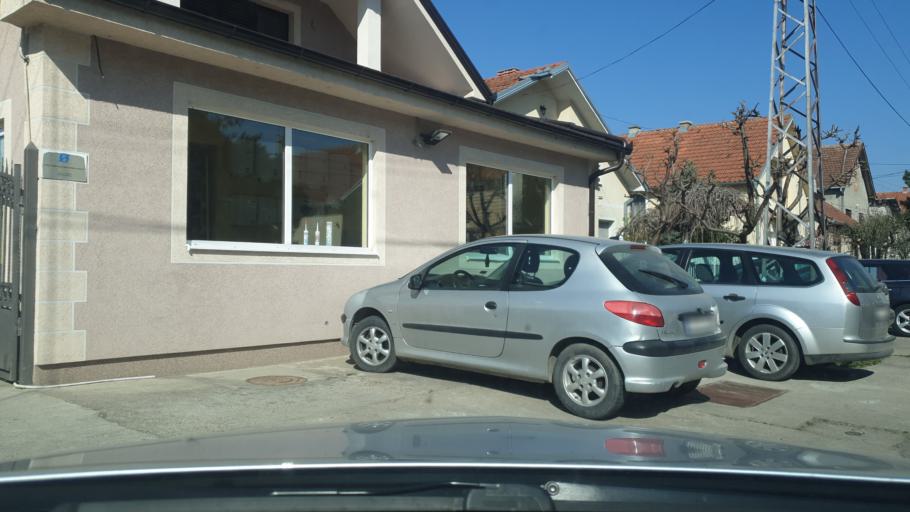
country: RS
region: Autonomna Pokrajina Vojvodina
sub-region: Sremski Okrug
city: Stara Pazova
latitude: 44.9919
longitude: 20.1422
